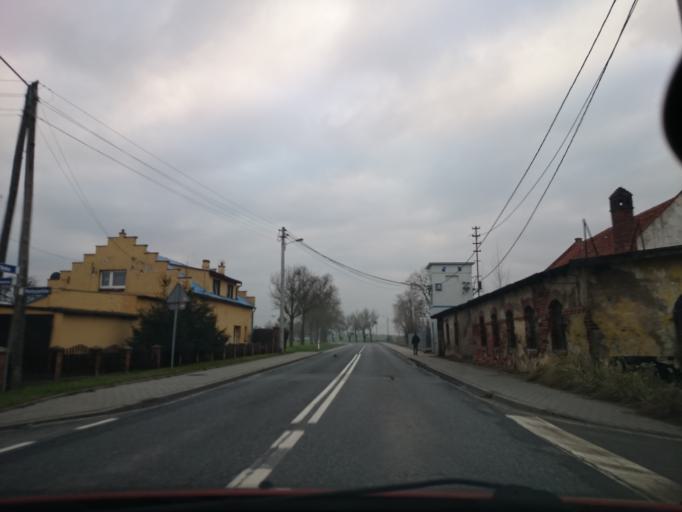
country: PL
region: Opole Voivodeship
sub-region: Powiat nyski
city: Sidzina
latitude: 50.5721
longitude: 17.4471
